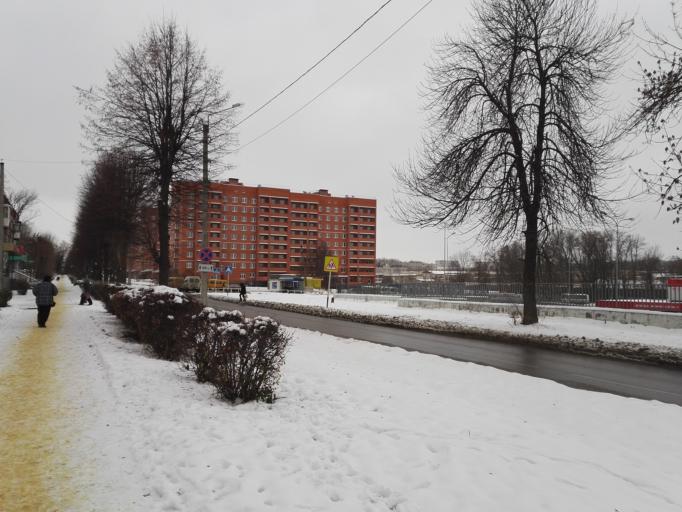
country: RU
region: Tula
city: Novomoskovsk
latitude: 54.0101
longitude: 38.3159
